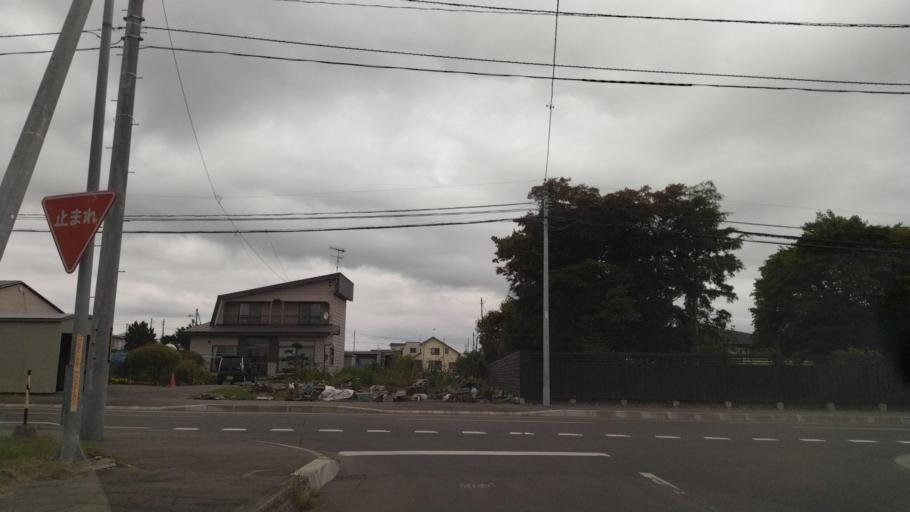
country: JP
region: Hokkaido
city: Otofuke
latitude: 43.2343
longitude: 143.2979
